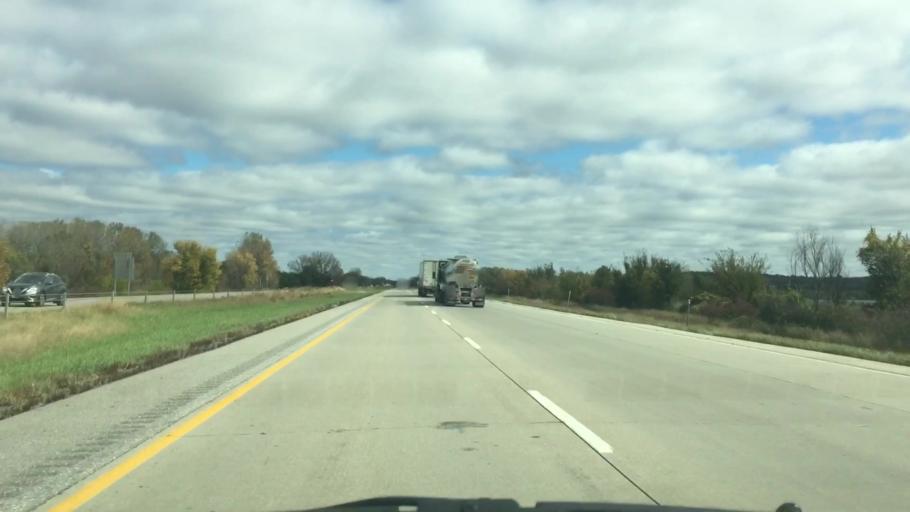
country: US
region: Iowa
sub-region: Jasper County
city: Colfax
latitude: 41.6932
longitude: -93.2412
